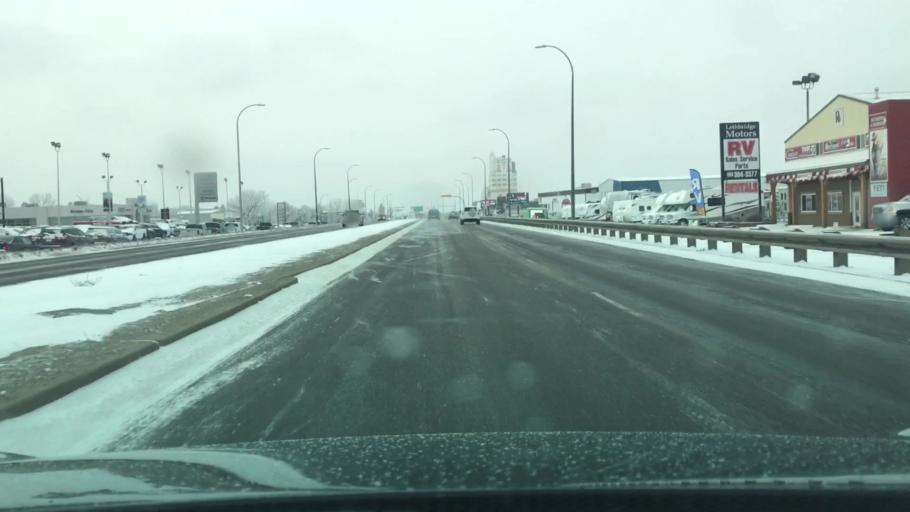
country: CA
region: Alberta
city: Lethbridge
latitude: 49.6983
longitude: -112.7908
